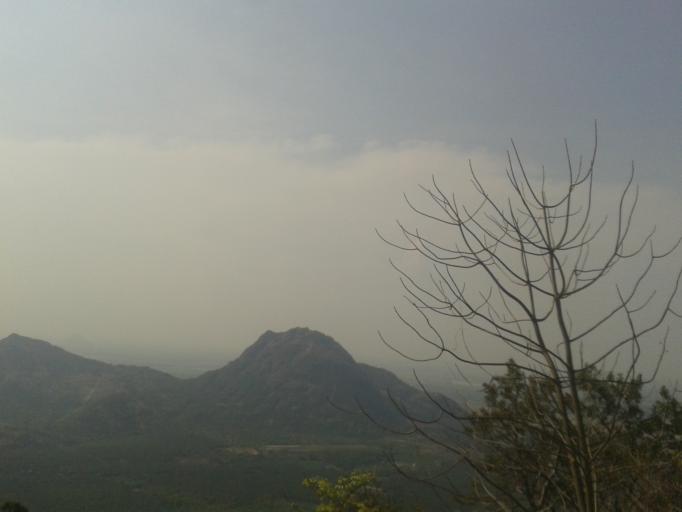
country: IN
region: Tamil Nadu
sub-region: Dindigul
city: Palani
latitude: 10.3605
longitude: 77.5289
